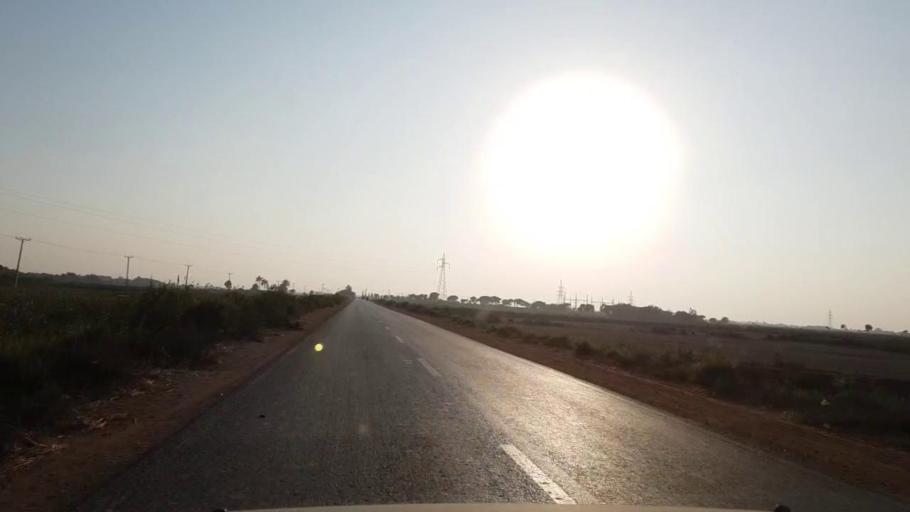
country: PK
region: Sindh
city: Daro Mehar
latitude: 24.6310
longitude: 68.1046
